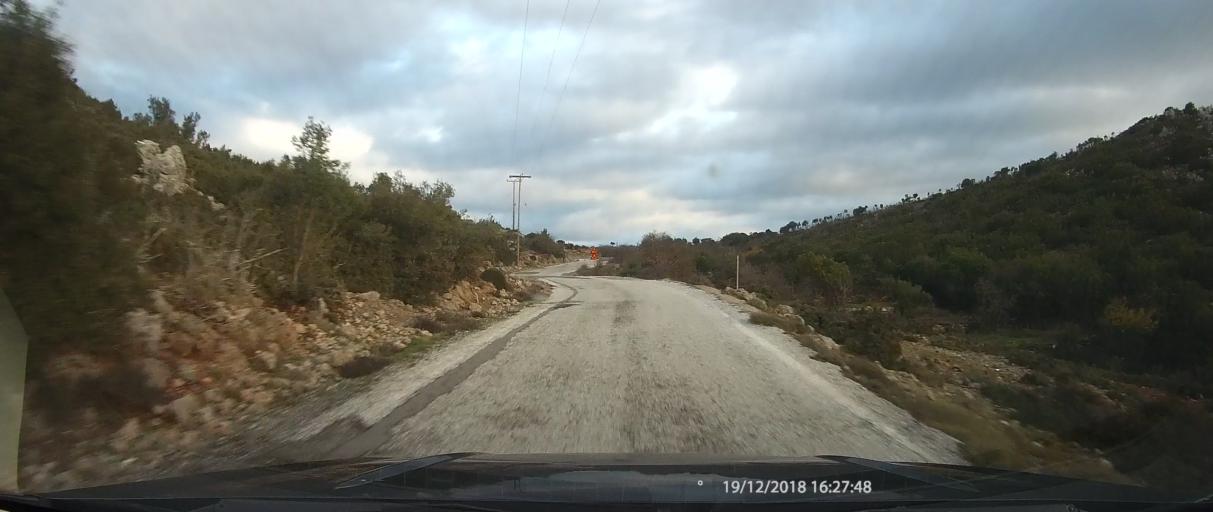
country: GR
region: Peloponnese
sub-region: Nomos Lakonias
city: Kato Glikovrisi
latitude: 36.9615
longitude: 22.8599
